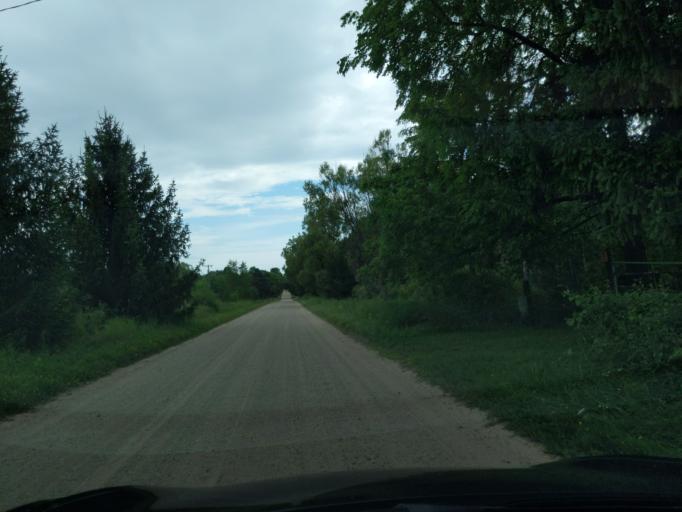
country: US
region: Michigan
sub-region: Clare County
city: Harrison
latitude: 43.9969
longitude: -85.0084
